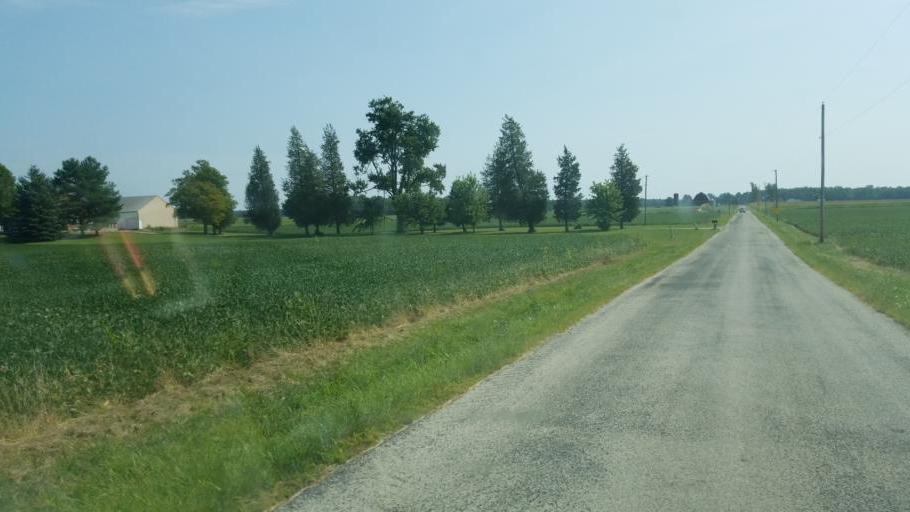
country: US
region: Ohio
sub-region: Crawford County
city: Crestline
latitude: 40.8249
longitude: -82.7062
